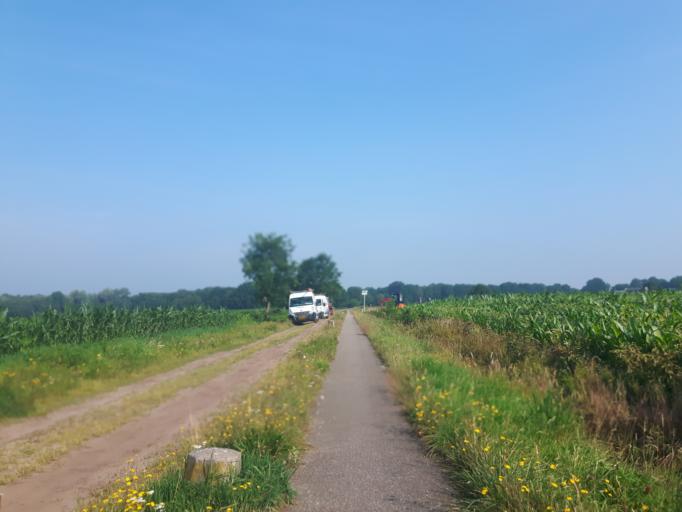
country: NL
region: Overijssel
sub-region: Gemeente Haaksbergen
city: Haaksbergen
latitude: 52.1885
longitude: 6.7896
